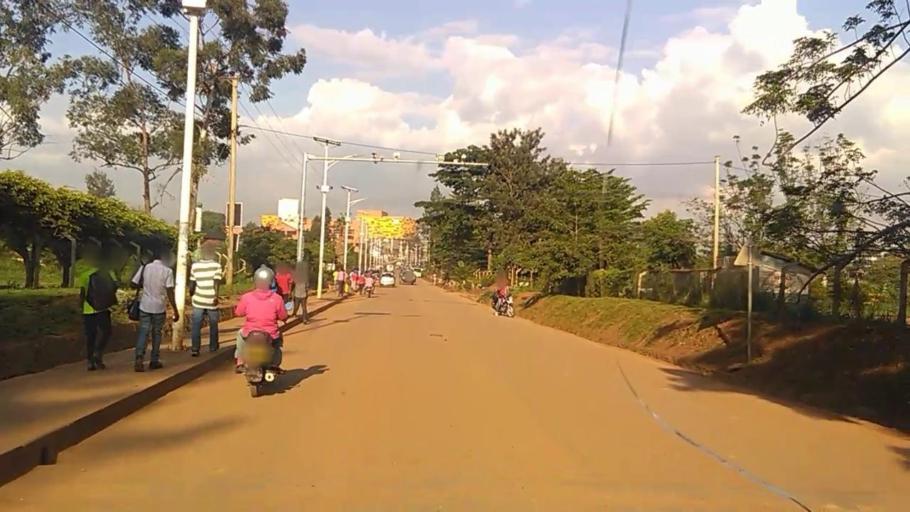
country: UG
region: Central Region
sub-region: Kampala District
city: Kampala
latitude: 0.3087
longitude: 32.5903
